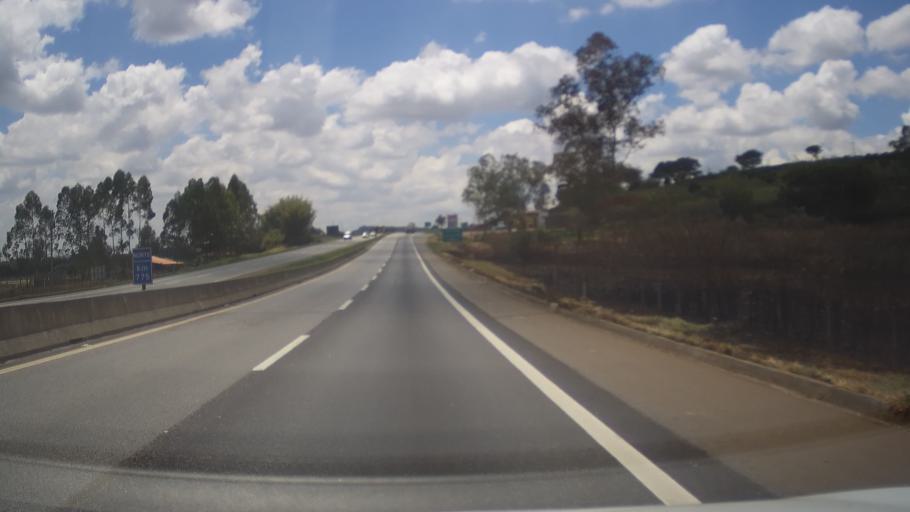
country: BR
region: Minas Gerais
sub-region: Campanha
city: Campanha
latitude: -21.7900
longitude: -45.4453
